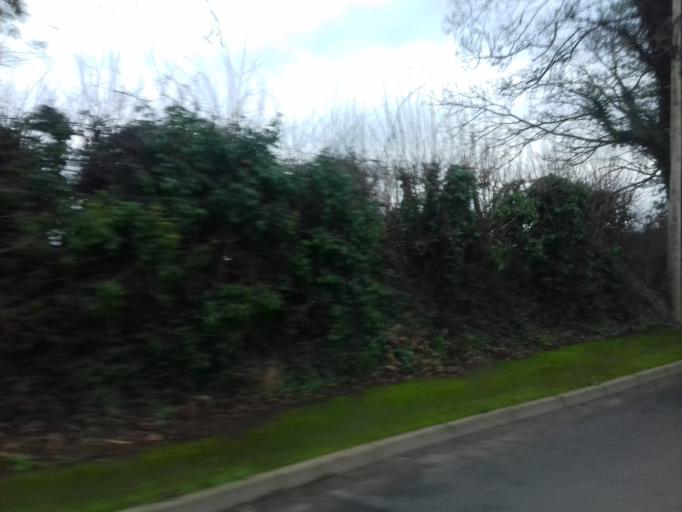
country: IE
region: Leinster
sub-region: An Mhi
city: Duleek
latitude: 53.6907
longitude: -6.4176
